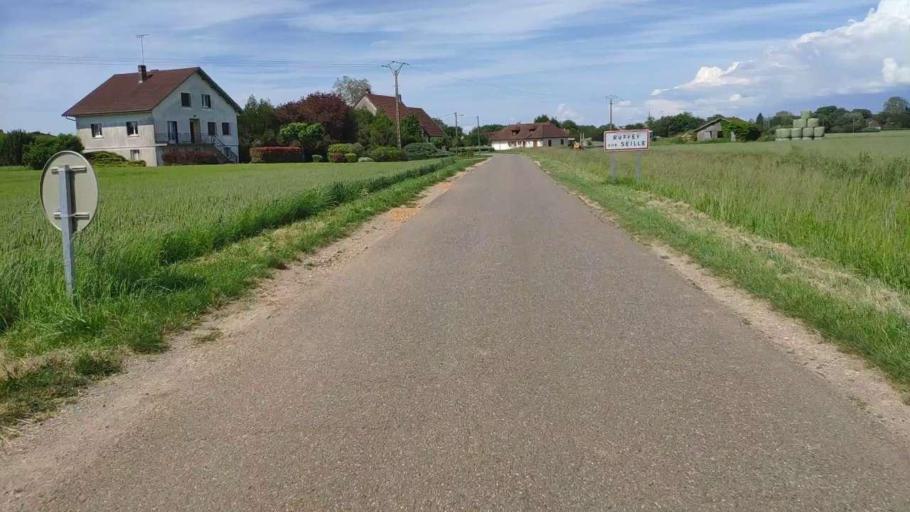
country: FR
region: Franche-Comte
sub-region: Departement du Jura
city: Bletterans
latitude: 46.7381
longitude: 5.4853
